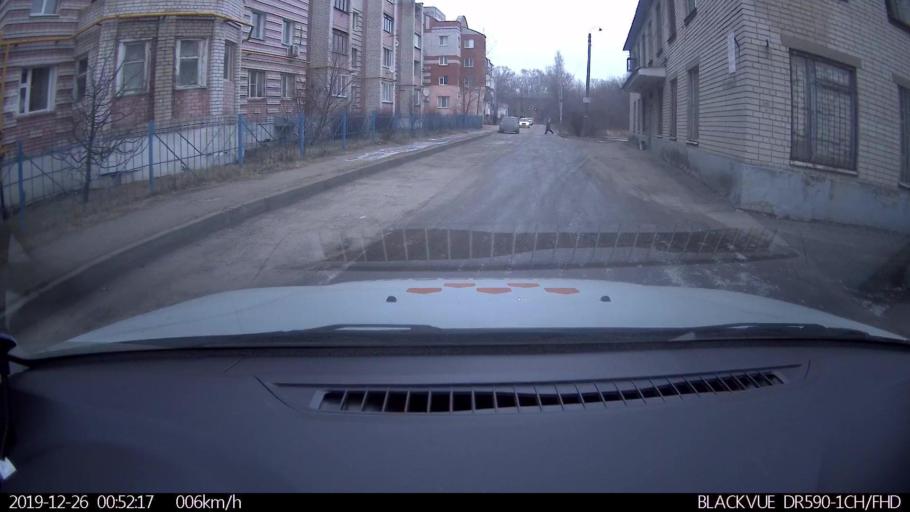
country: RU
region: Nizjnij Novgorod
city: Nizhniy Novgorod
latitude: 56.3008
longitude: 43.8804
